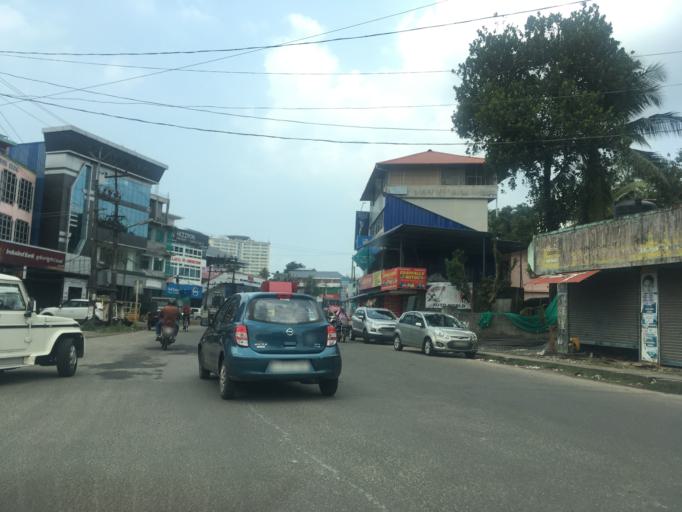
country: IN
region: Kerala
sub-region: Ernakulam
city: Elur
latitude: 10.0261
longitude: 76.3123
